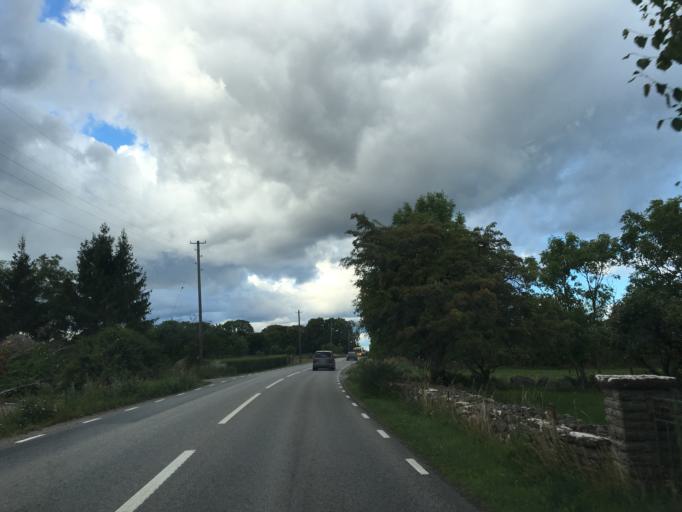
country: SE
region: Kalmar
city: Faerjestaden
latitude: 56.6417
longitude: 16.5162
